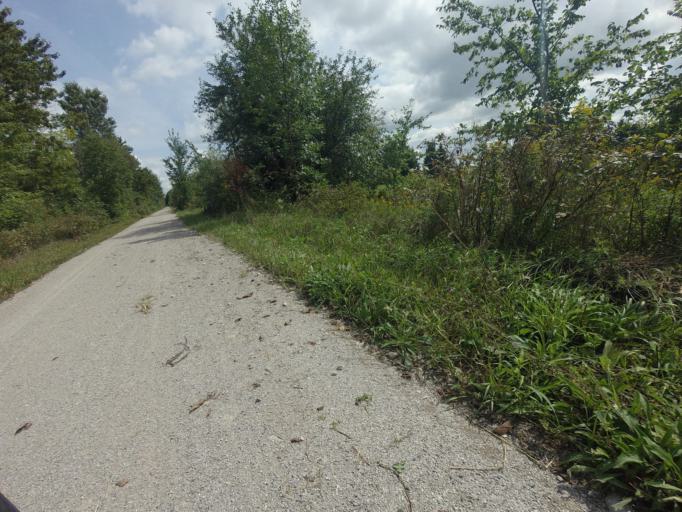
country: CA
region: Ontario
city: North Perth
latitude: 43.5636
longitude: -80.9916
